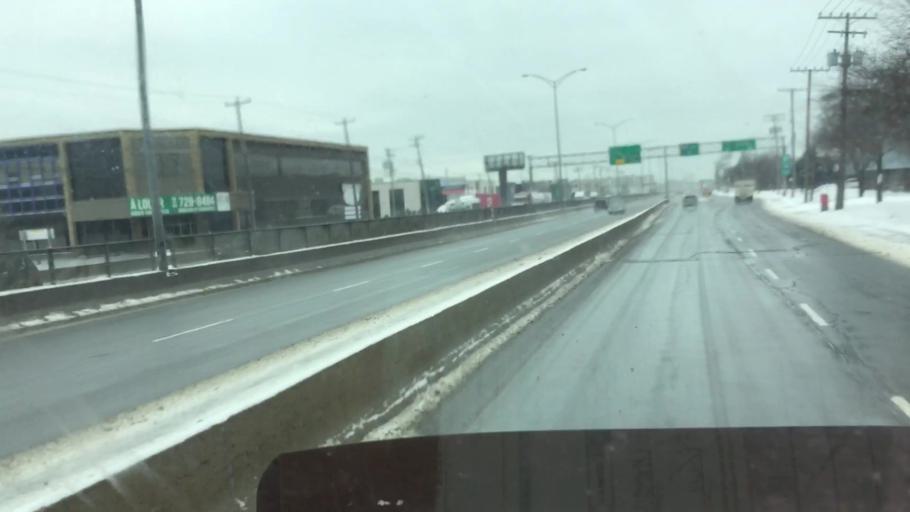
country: CA
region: Quebec
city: Dorval
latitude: 45.4678
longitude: -73.7157
